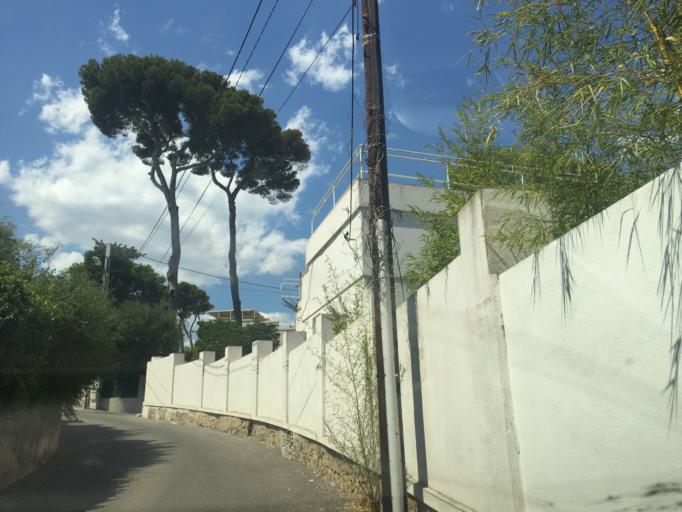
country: FR
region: Provence-Alpes-Cote d'Azur
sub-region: Departement des Alpes-Maritimes
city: Antibes
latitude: 43.5560
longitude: 7.1320
